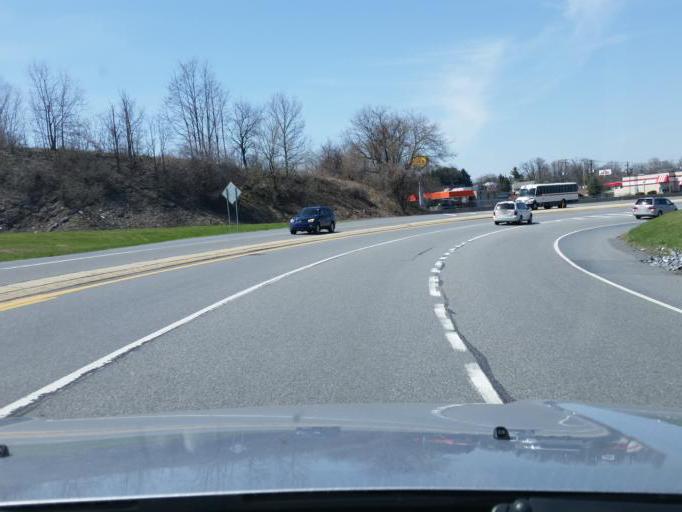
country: US
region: Pennsylvania
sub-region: Dauphin County
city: Hummelstown
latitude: 40.2662
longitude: -76.6877
